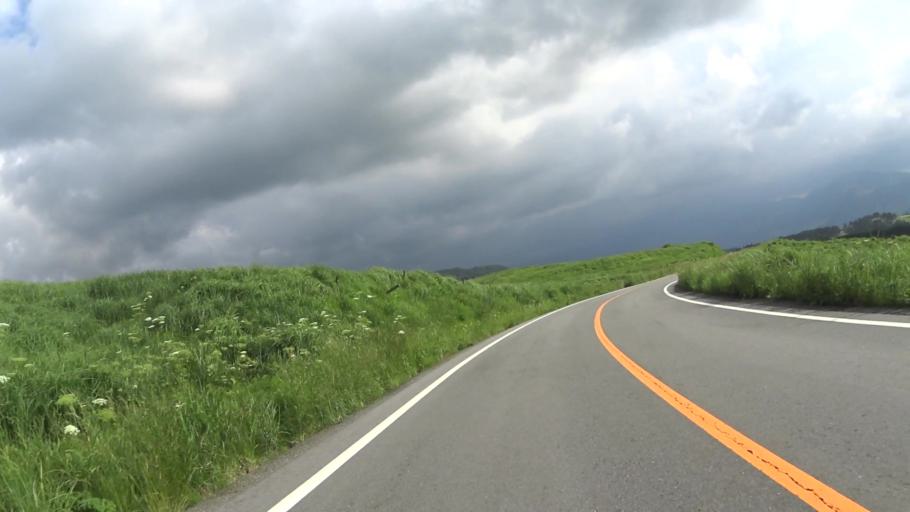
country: JP
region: Kumamoto
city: Aso
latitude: 32.9041
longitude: 131.0302
